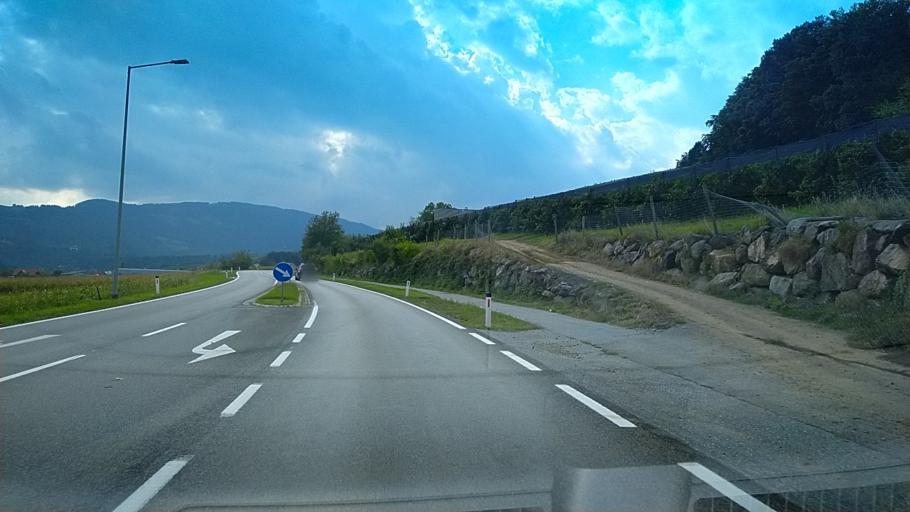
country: AT
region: Styria
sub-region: Politischer Bezirk Deutschlandsberg
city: Hollenegg
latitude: 46.7747
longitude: 15.2201
